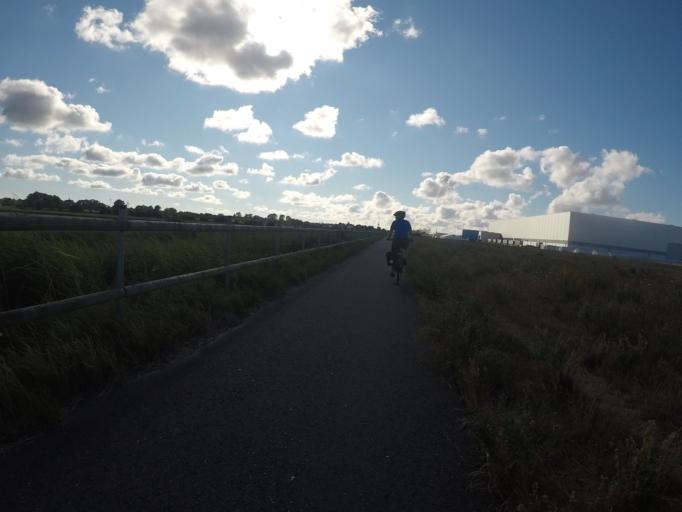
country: DE
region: Lower Saxony
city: Cuxhaven
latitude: 53.8378
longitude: 8.7587
